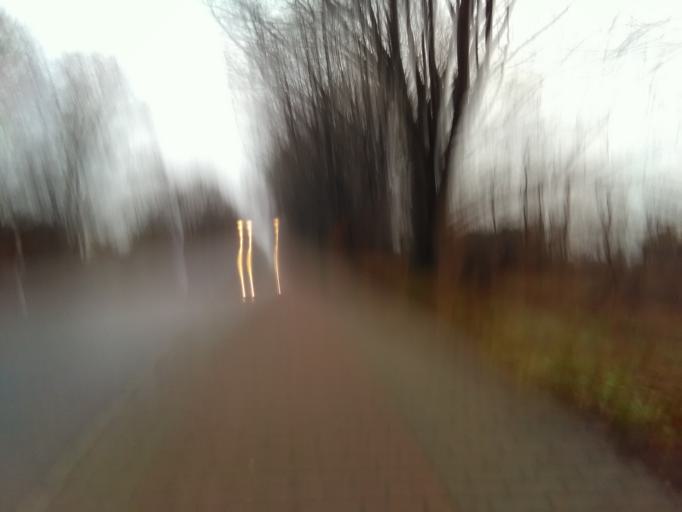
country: DE
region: Schleswig-Holstein
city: Quickborn
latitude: 53.7256
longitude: 9.9294
